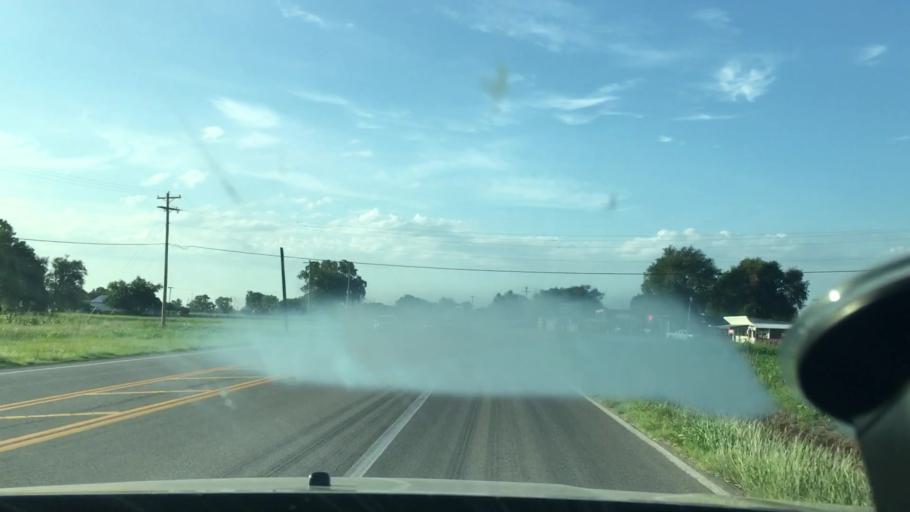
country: US
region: Oklahoma
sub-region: Garvin County
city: Wynnewood
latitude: 34.6526
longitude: -97.2009
